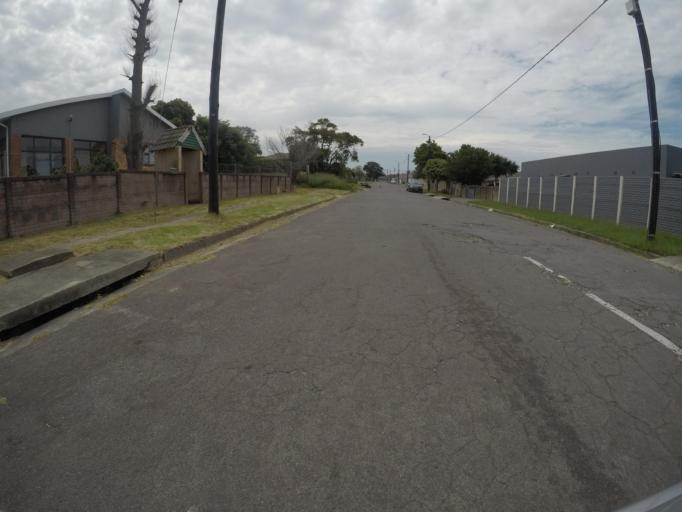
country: ZA
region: Eastern Cape
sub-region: Buffalo City Metropolitan Municipality
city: East London
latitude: -32.9732
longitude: 27.8685
